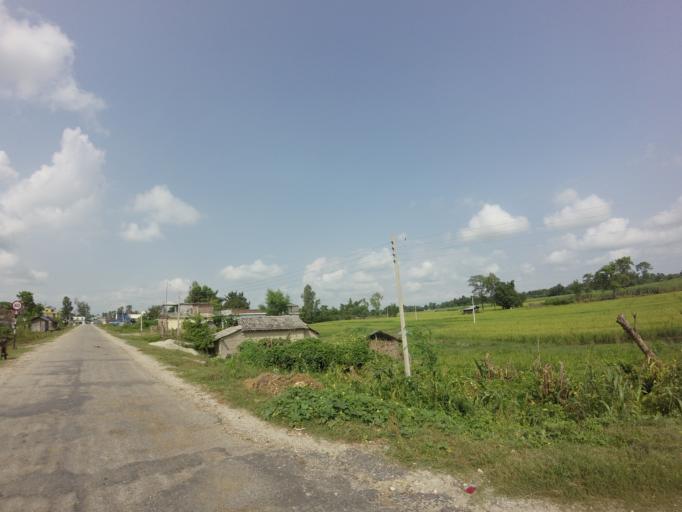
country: NP
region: Far Western
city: Tikapur
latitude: 28.4576
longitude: 81.0766
